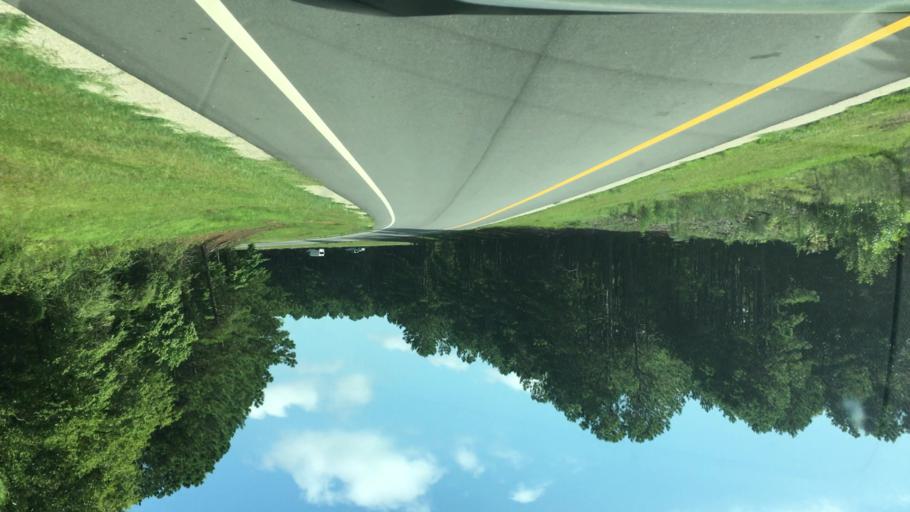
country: US
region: North Carolina
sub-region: Cumberland County
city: Fayetteville
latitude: 34.9772
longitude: -78.8592
